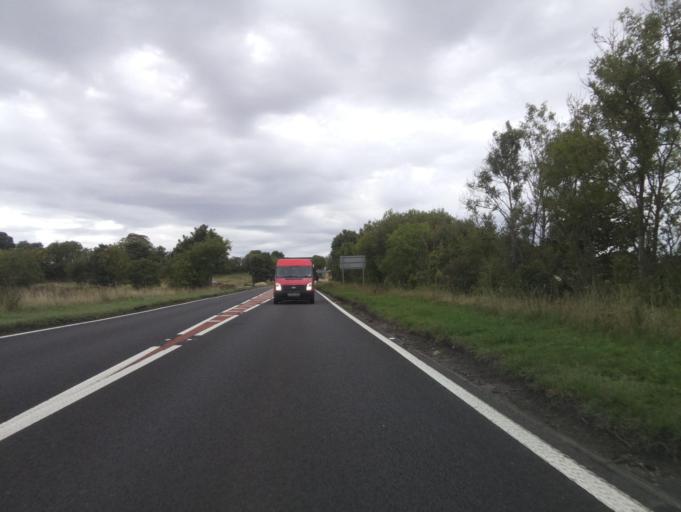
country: GB
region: Scotland
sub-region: Fife
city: High Valleyfield
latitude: 56.0645
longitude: -3.6103
